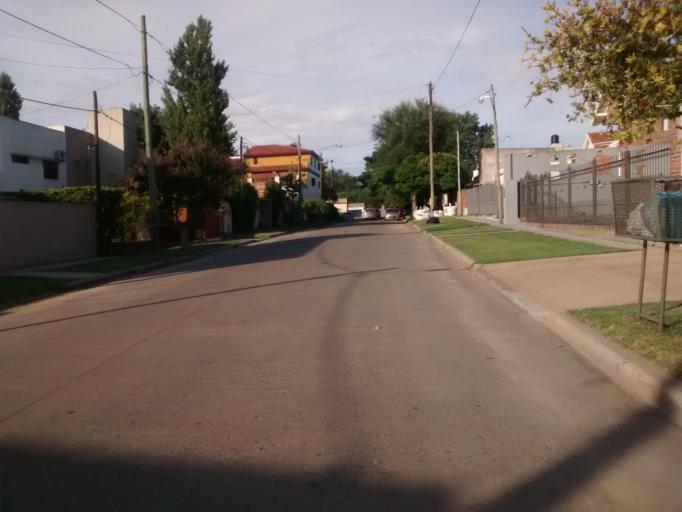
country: AR
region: Buenos Aires
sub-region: Partido de La Plata
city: La Plata
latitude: -34.8554
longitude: -58.0782
